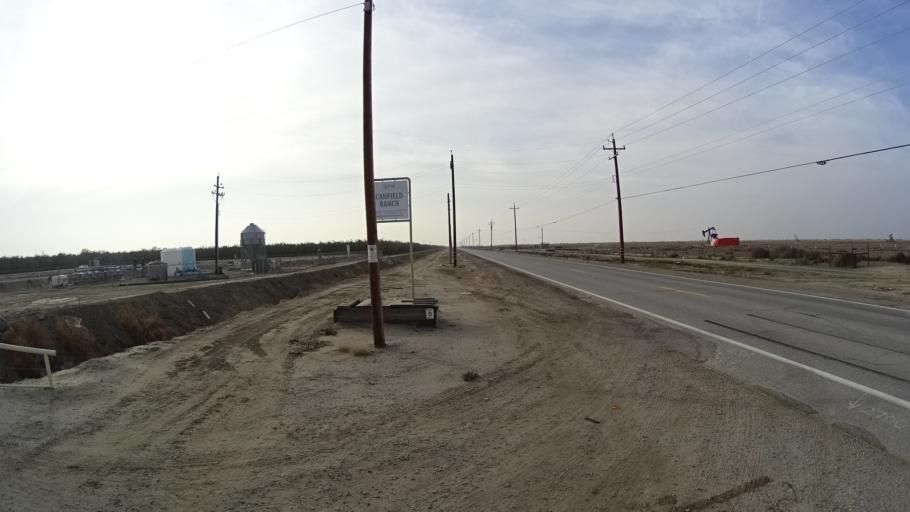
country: US
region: California
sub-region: Kern County
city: Rosedale
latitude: 35.2962
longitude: -119.1459
